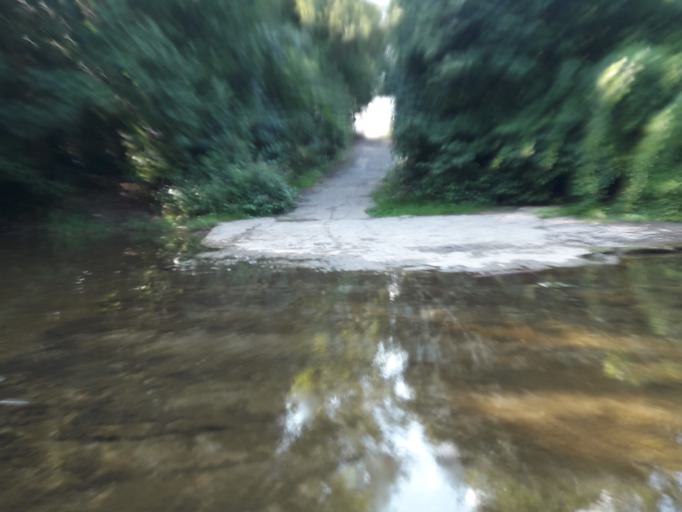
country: DE
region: North Rhine-Westphalia
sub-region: Regierungsbezirk Detmold
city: Paderborn
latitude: 51.7200
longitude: 8.7148
